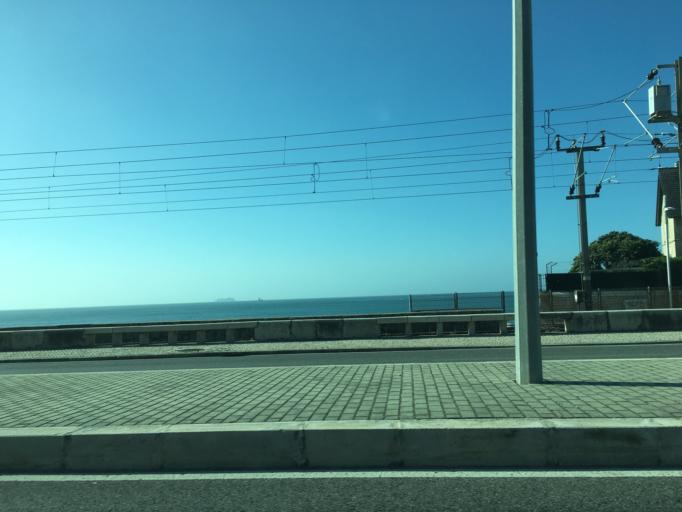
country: PT
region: Lisbon
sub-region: Cascais
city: Monte Estoril
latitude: 38.7018
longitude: -9.4129
